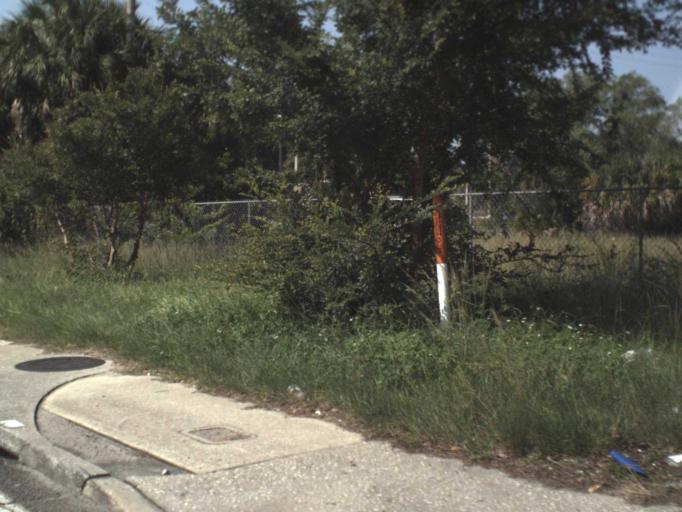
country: US
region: Florida
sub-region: Hillsborough County
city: Carrollwood
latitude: 28.0414
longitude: -82.4595
